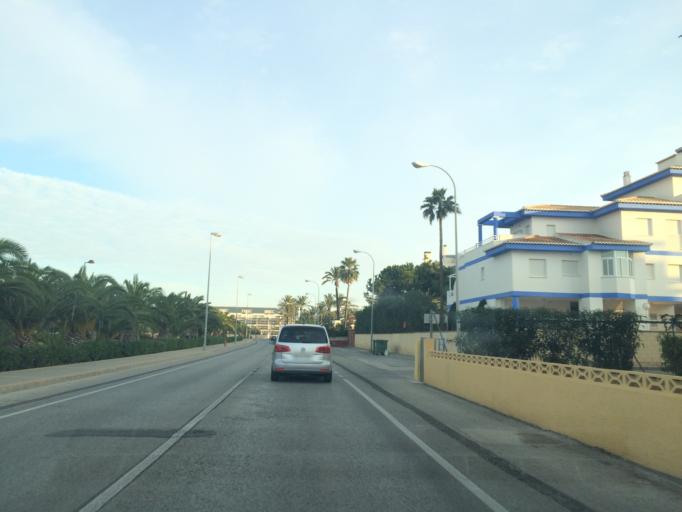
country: ES
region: Valencia
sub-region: Provincia de Alicante
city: Denia
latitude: 38.8529
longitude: 0.0900
